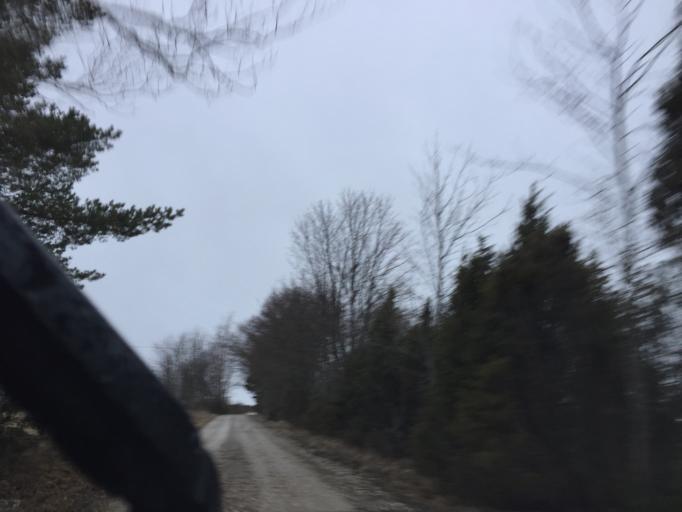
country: EE
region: Laeaene
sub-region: Haapsalu linn
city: Haapsalu
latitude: 58.6850
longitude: 23.5082
